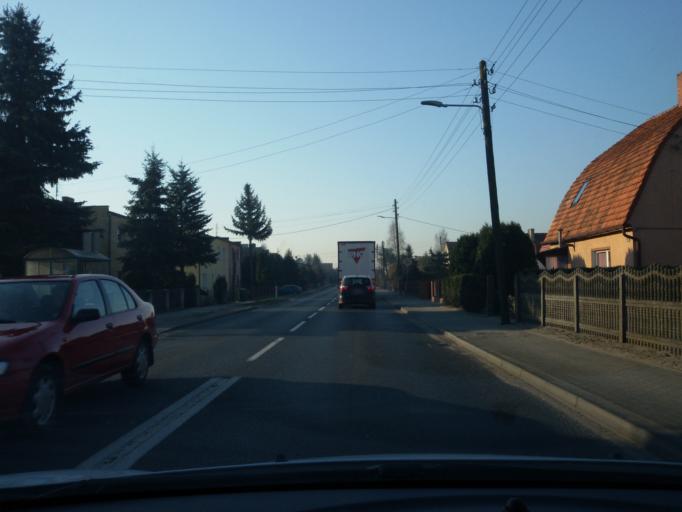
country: PL
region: Lubusz
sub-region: Powiat wschowski
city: Wschowa
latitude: 51.8110
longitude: 16.3288
